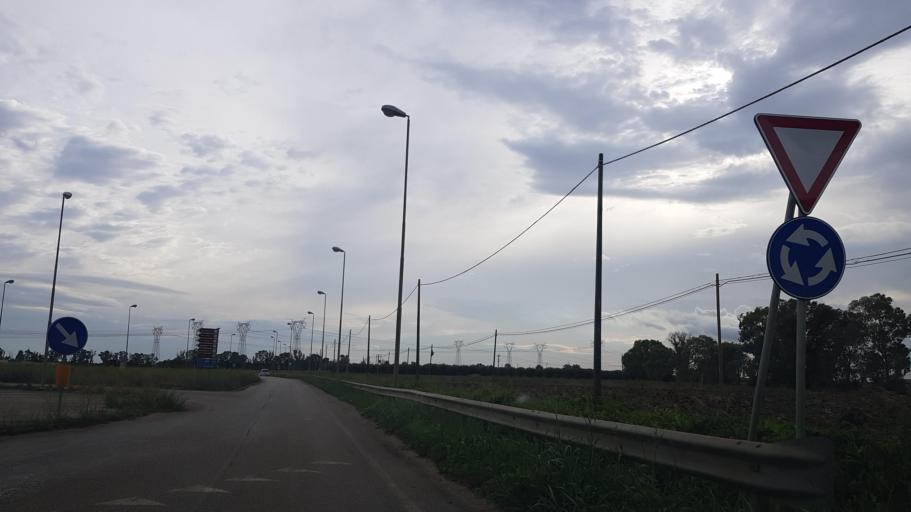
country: IT
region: Apulia
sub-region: Provincia di Brindisi
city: Tuturano
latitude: 40.5618
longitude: 18.0081
